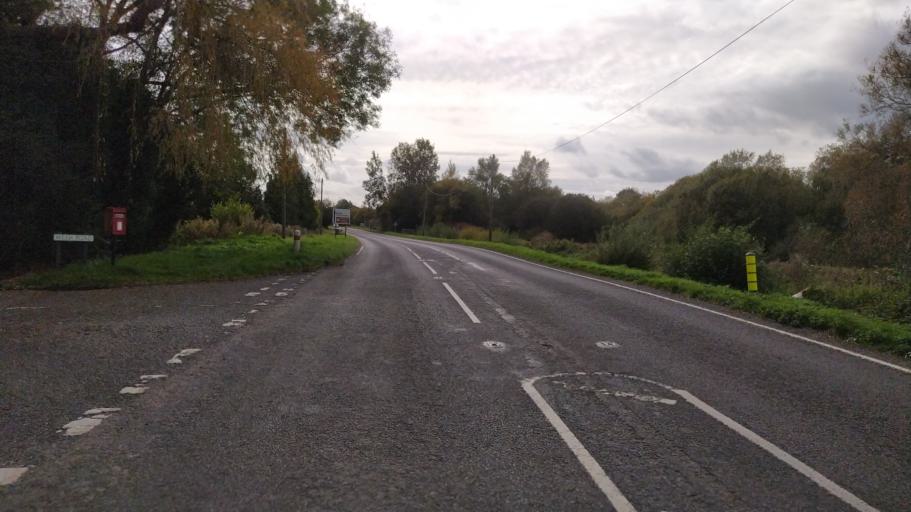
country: GB
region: England
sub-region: Hampshire
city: Romsey
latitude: 51.0388
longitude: -1.5243
